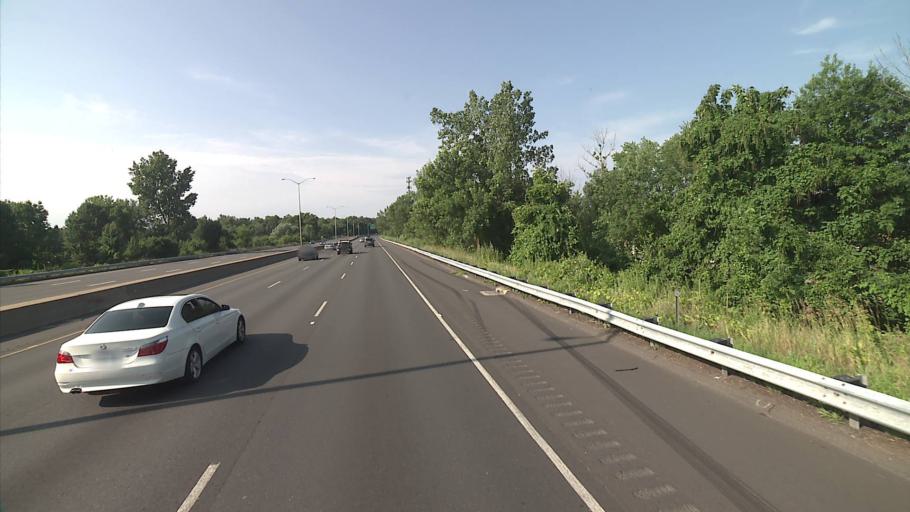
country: US
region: Connecticut
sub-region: Hartford County
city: Enfield
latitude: 41.9633
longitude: -72.5908
